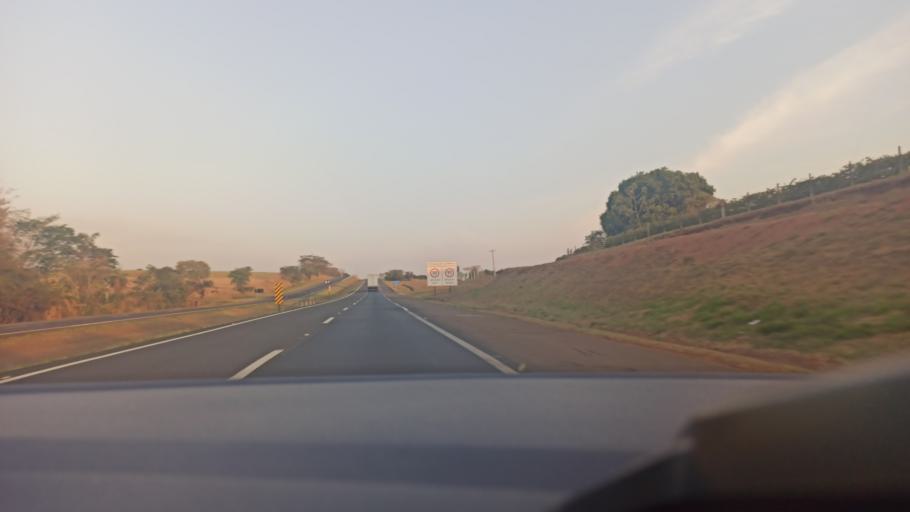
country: BR
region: Sao Paulo
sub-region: Santa Adelia
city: Santa Adelia
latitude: -21.3987
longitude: -48.7097
